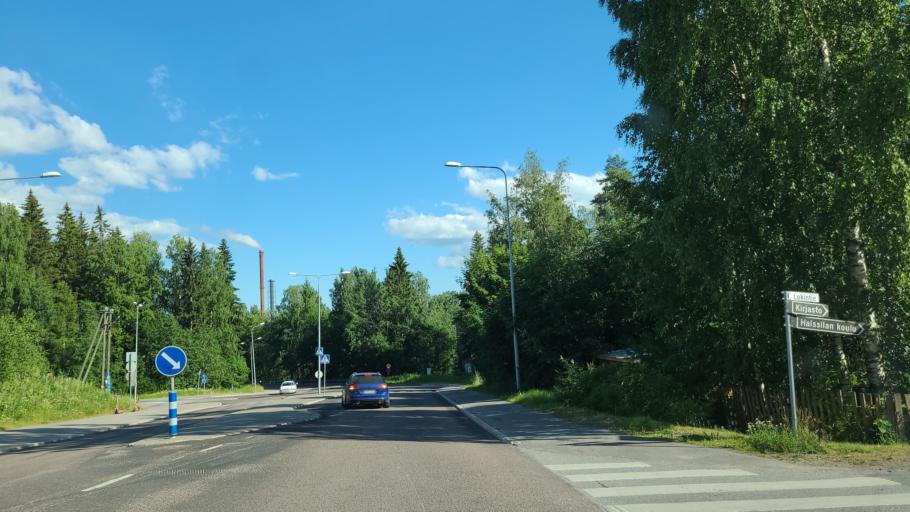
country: FI
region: Central Finland
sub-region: Jyvaeskylae
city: Jyvaeskylae
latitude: 62.2427
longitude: 25.7994
